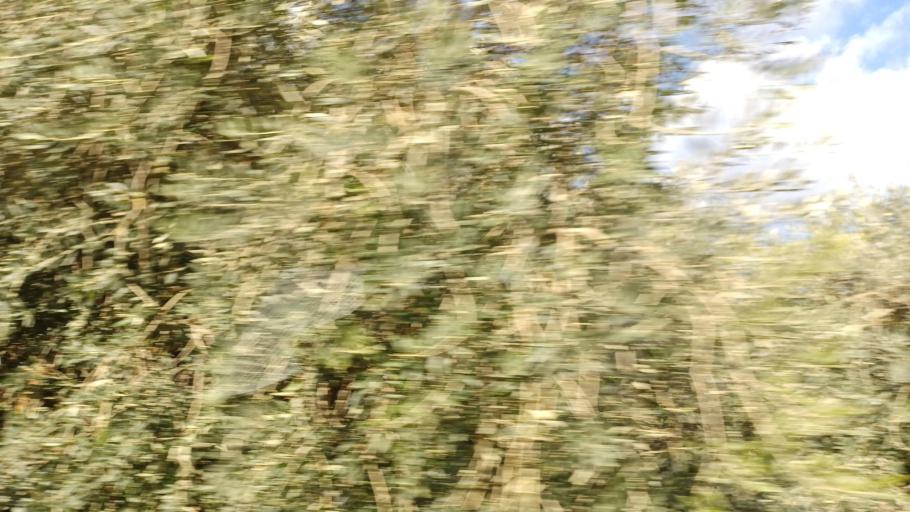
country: CY
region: Pafos
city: Polis
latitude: 35.1285
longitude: 32.5196
